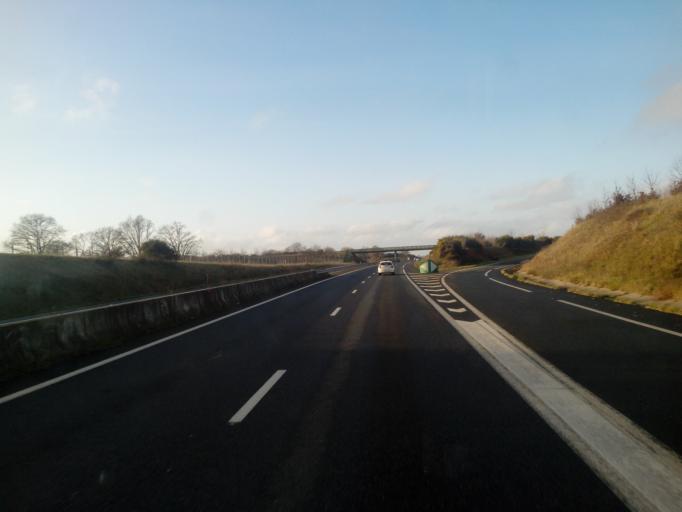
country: FR
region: Pays de la Loire
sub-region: Departement de Maine-et-Loire
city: La Tessoualle
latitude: 46.9872
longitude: -0.8404
